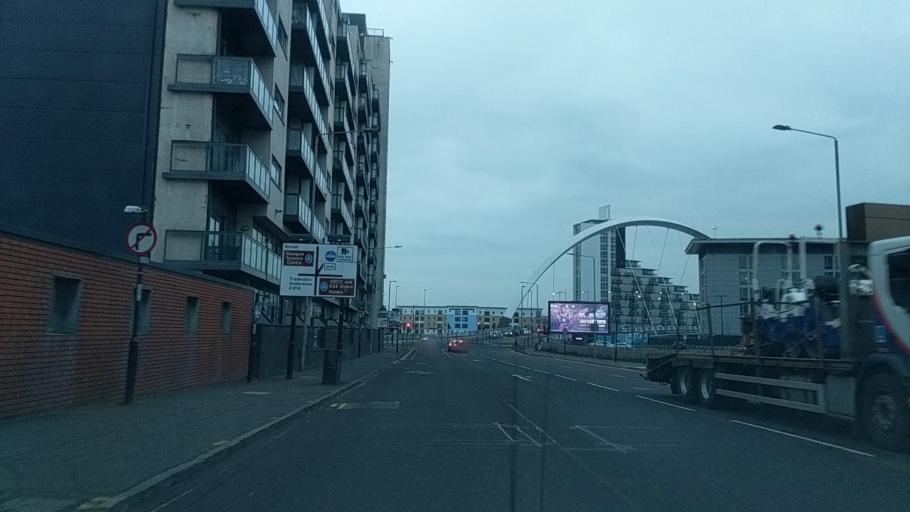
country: GB
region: Scotland
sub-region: Glasgow City
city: Glasgow
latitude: 55.8589
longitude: -4.2814
